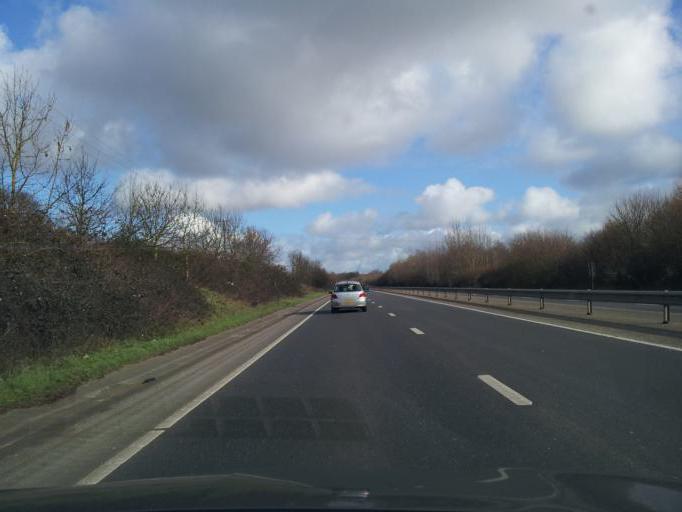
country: GB
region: England
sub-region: Norfolk
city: Diss
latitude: 52.3679
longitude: 1.1546
